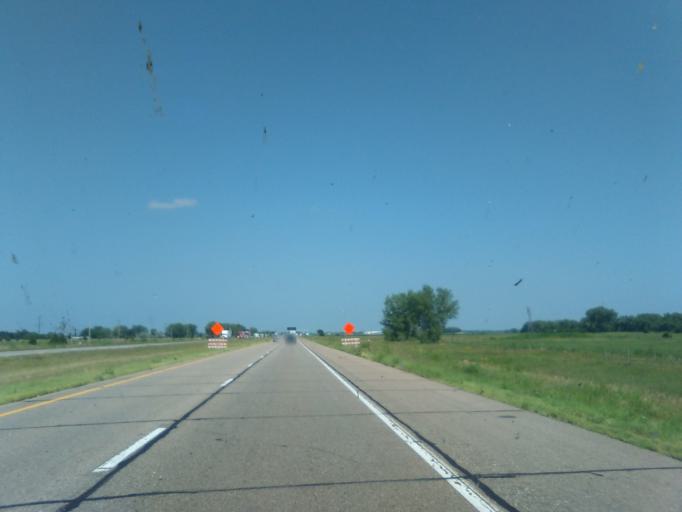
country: US
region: Nebraska
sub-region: Buffalo County
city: Kearney
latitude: 40.6702
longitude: -99.1330
